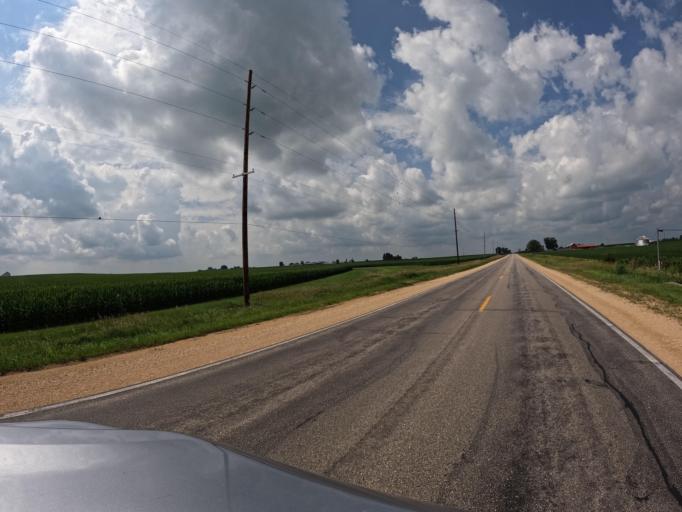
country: US
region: Iowa
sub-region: Clinton County
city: Camanche
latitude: 41.7736
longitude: -90.3548
